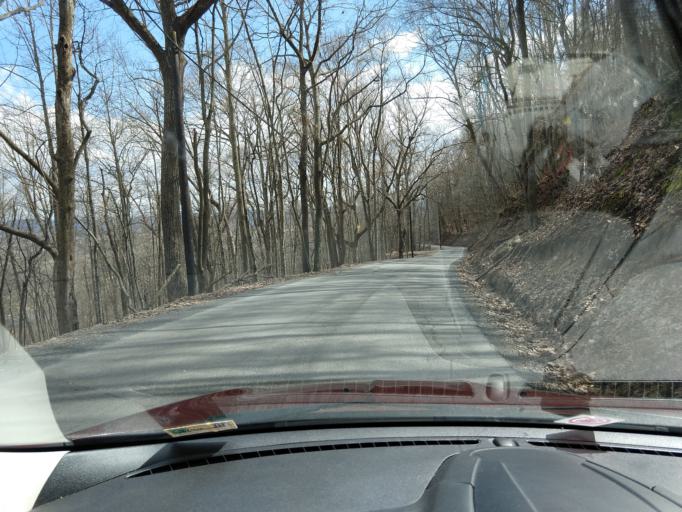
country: US
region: West Virginia
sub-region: Greenbrier County
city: Lewisburg
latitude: 37.8263
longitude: -80.5138
